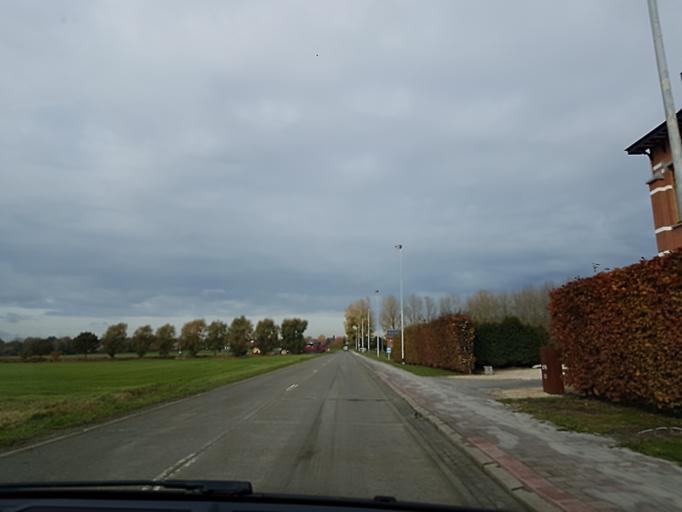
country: BE
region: Flanders
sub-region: Provincie Antwerpen
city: Lint
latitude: 51.1391
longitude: 4.4926
